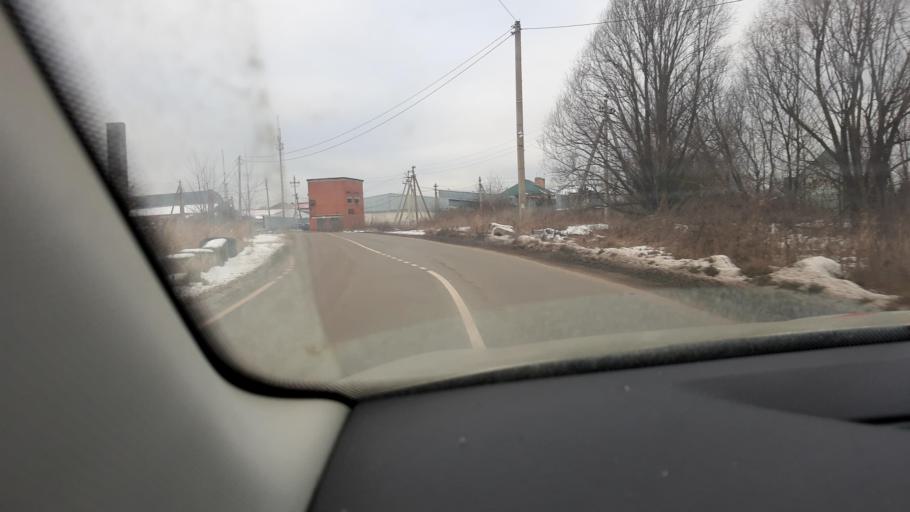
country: RU
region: Moskovskaya
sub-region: Leninskiy Rayon
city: Molokovo
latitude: 55.4887
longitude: 37.8587
